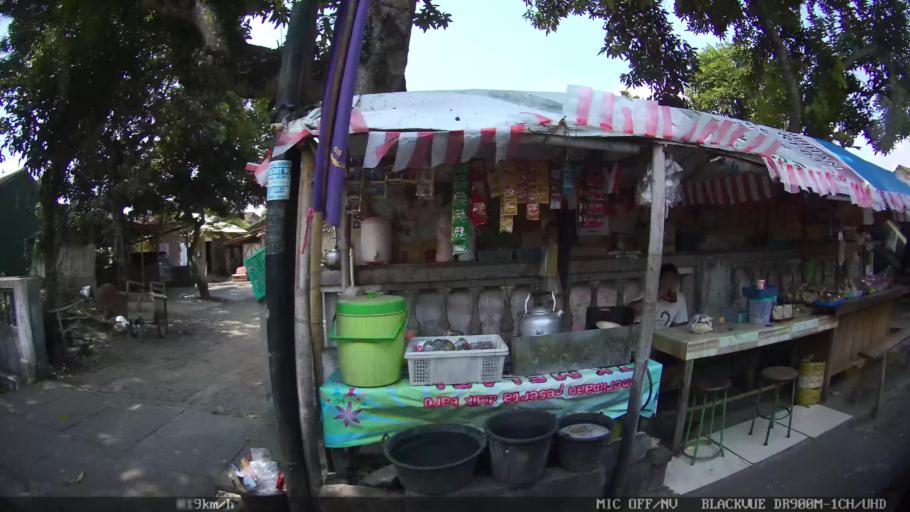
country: ID
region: Daerah Istimewa Yogyakarta
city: Yogyakarta
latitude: -7.8193
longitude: 110.4041
